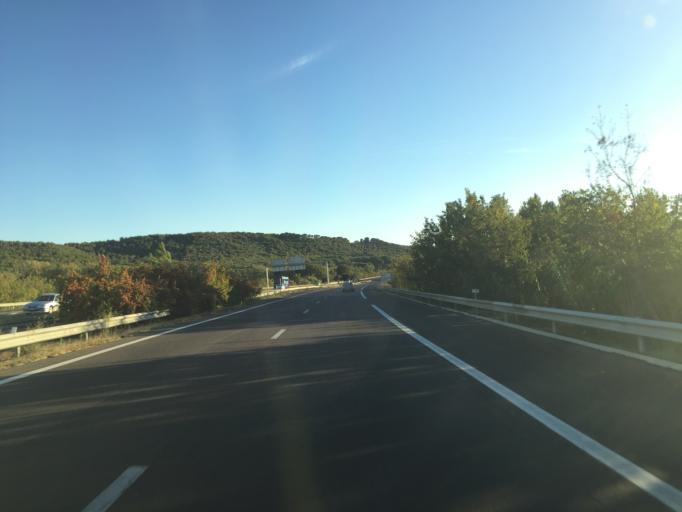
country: FR
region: Provence-Alpes-Cote d'Azur
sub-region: Departement des Bouches-du-Rhone
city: Coudoux
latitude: 43.5491
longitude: 5.2302
